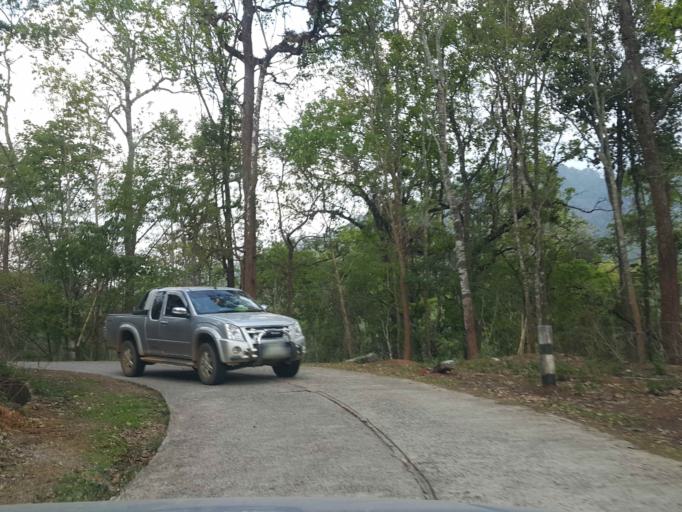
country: TH
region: Chiang Mai
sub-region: Amphoe Chiang Dao
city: Chiang Dao
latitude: 19.3841
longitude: 98.7755
